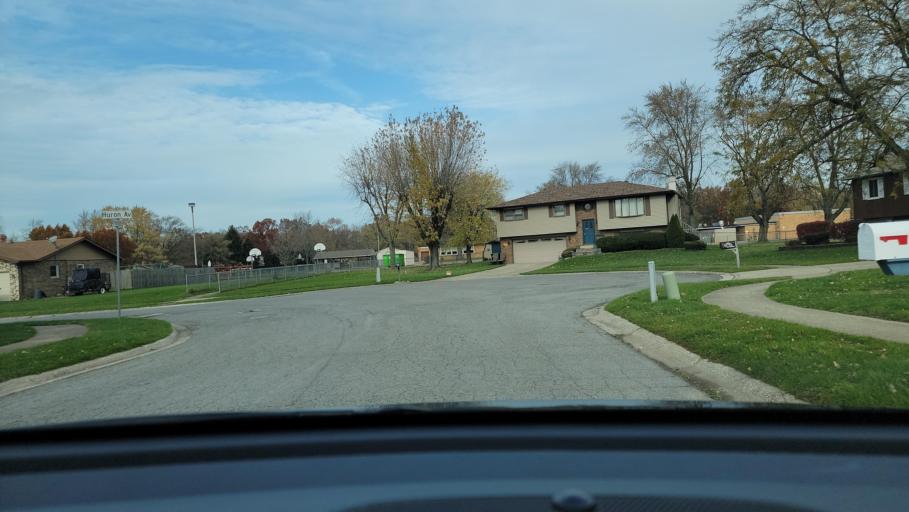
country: US
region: Indiana
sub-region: Porter County
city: Portage
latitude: 41.5821
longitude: -87.1457
